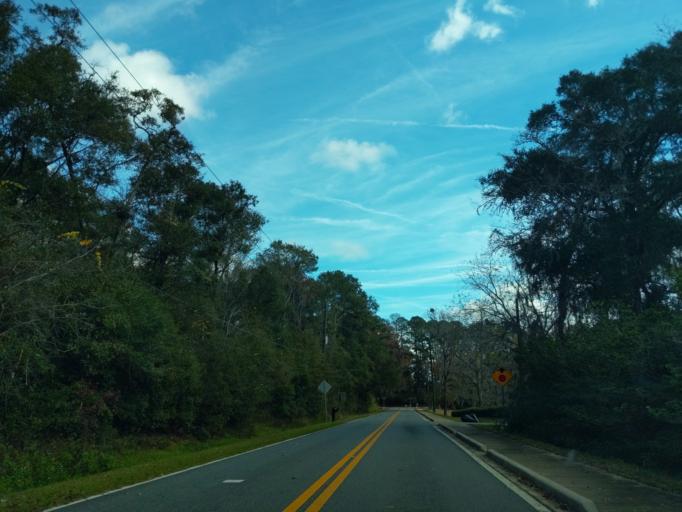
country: US
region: Florida
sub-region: Leon County
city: Tallahassee
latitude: 30.4685
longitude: -84.2121
